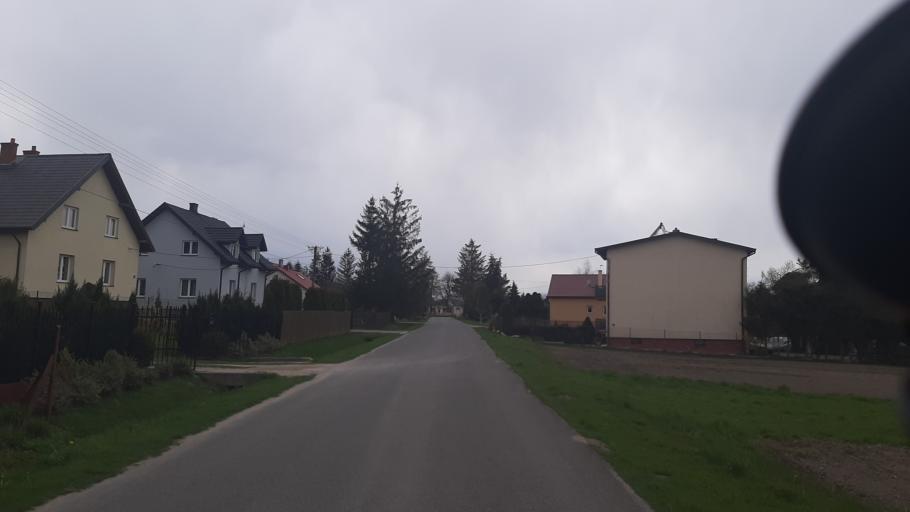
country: PL
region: Lublin Voivodeship
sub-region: Powiat lubelski
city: Niemce
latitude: 51.3624
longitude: 22.5336
